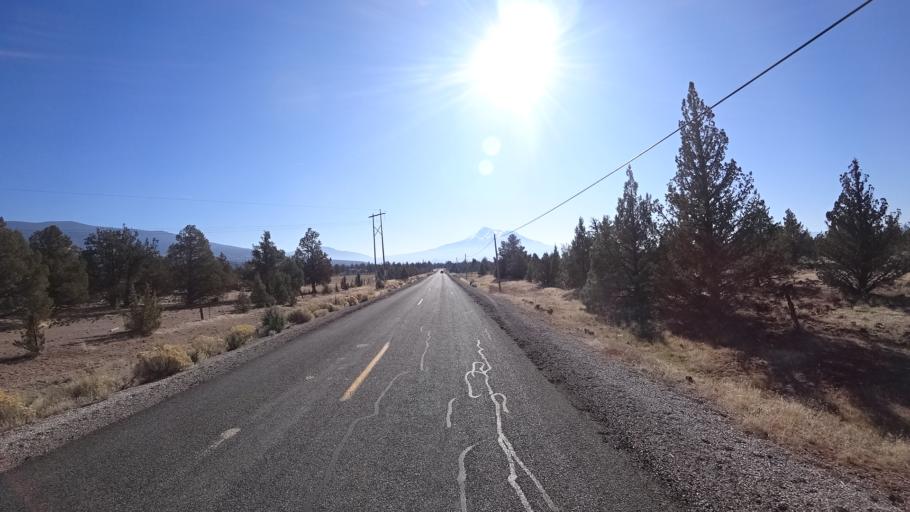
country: US
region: California
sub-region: Siskiyou County
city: Montague
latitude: 41.6564
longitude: -122.3643
